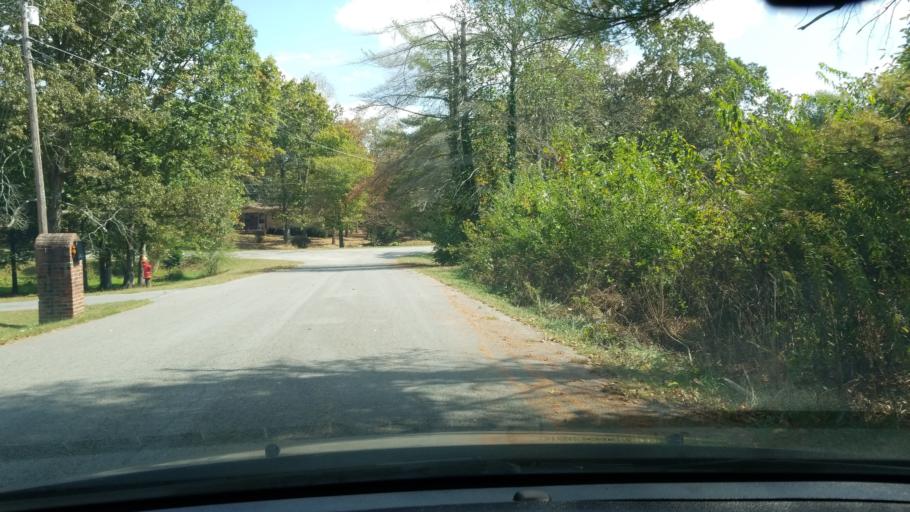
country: US
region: Tennessee
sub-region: Cumberland County
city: Crossville
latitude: 35.9611
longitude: -85.0686
